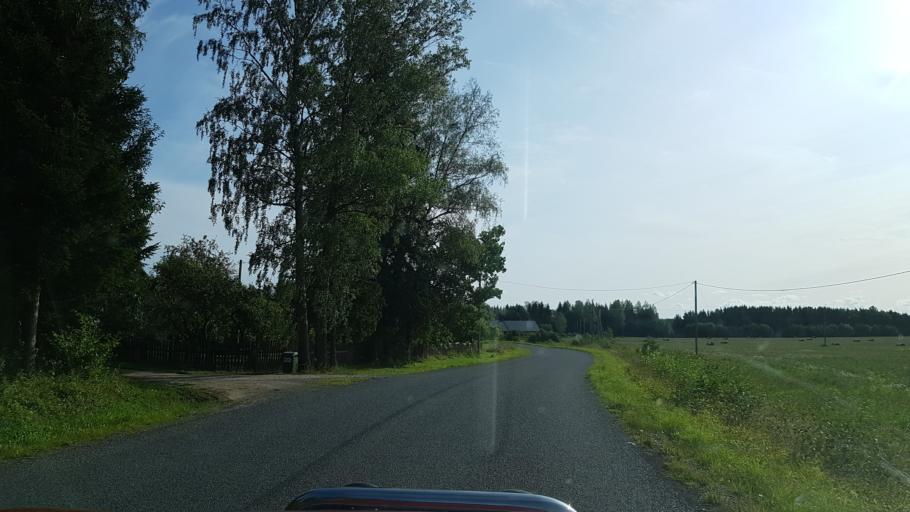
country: EE
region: Laeaene
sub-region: Lihula vald
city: Lihula
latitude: 58.3871
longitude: 24.0091
